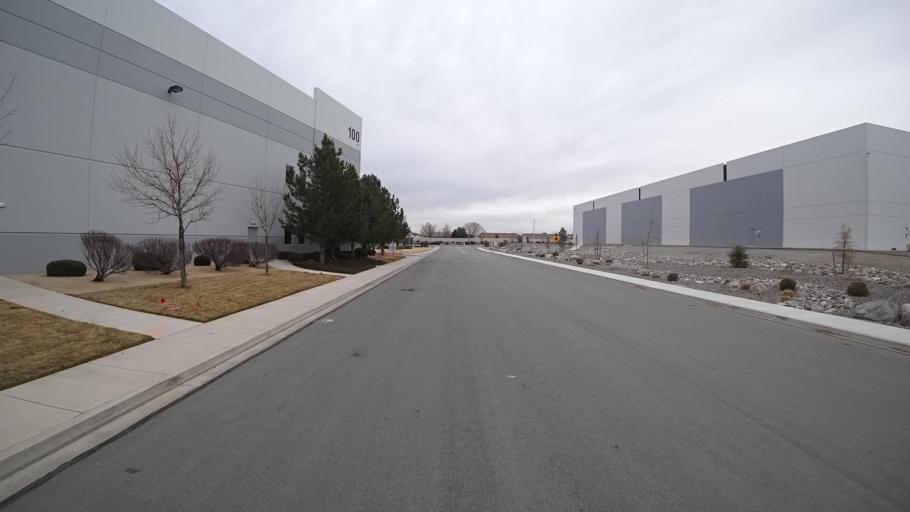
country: US
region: Nevada
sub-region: Washoe County
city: Spanish Springs
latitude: 39.6738
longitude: -119.7153
